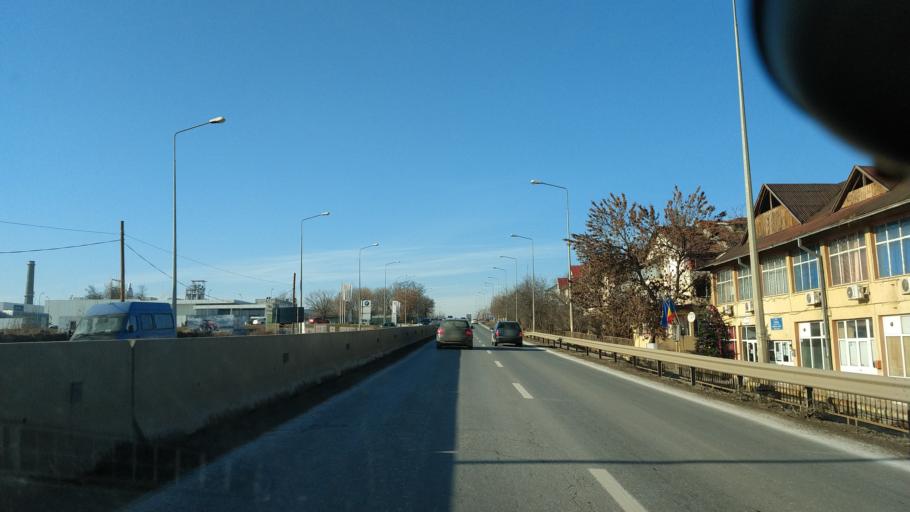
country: RO
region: Iasi
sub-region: Comuna Valea Lupului
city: Valea Lupului
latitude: 47.1756
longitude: 27.4970
